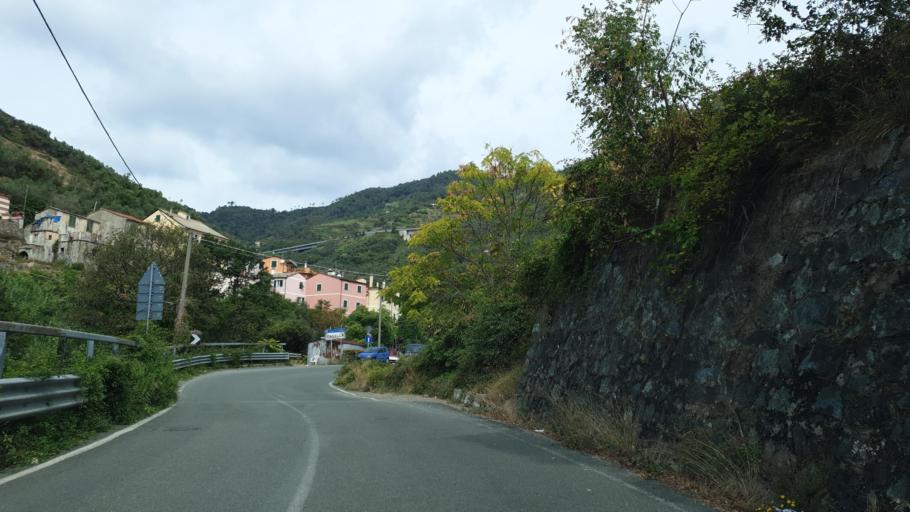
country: IT
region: Liguria
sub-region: Provincia di La Spezia
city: Levanto
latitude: 44.1914
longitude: 9.6259
